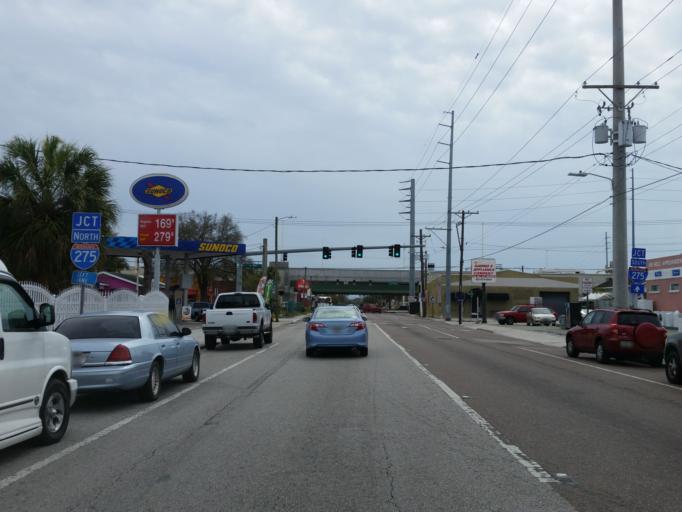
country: US
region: Florida
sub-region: Hillsborough County
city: Tampa
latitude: 27.9580
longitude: -82.4850
